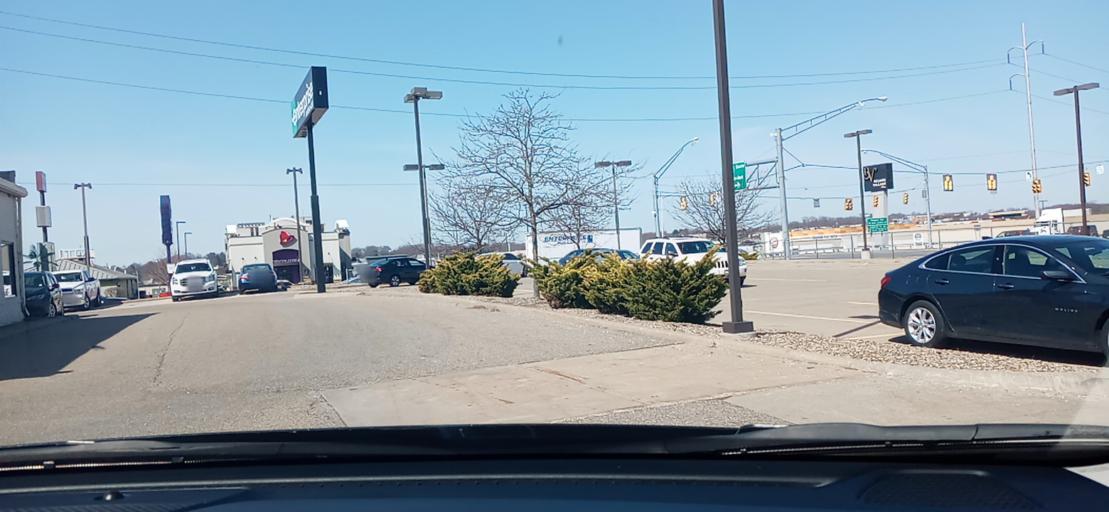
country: US
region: Ohio
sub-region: Stark County
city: North Canton
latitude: 40.8545
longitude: -81.4222
